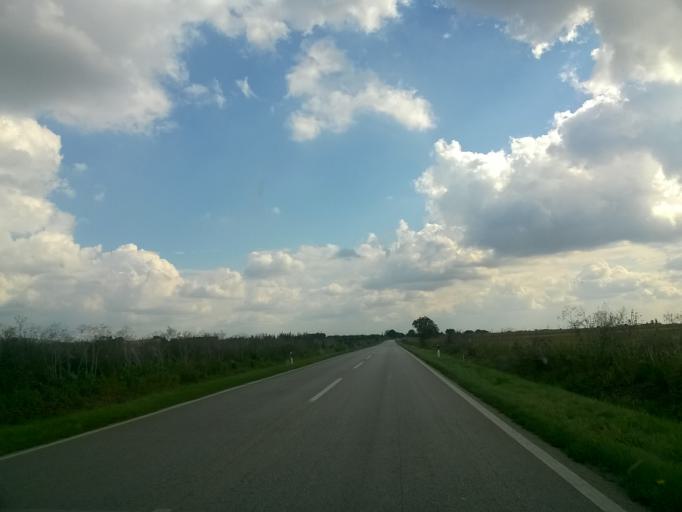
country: RS
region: Autonomna Pokrajina Vojvodina
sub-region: Juznobanatski Okrug
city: Vrsac
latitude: 45.1381
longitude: 21.2685
